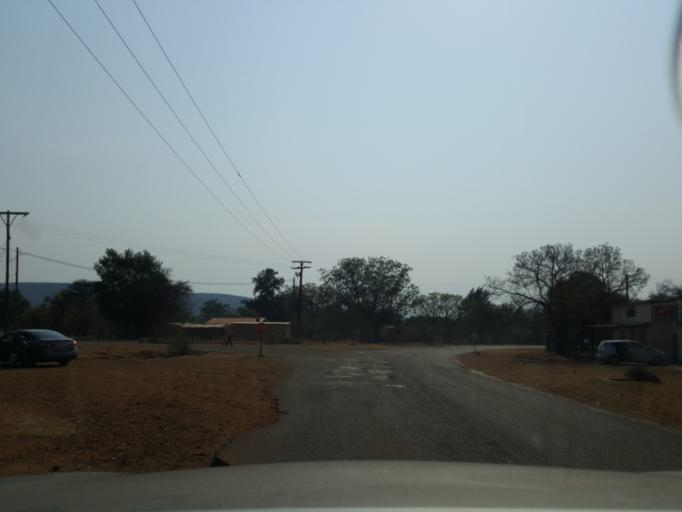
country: BW
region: South East
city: Lobatse
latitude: -25.3126
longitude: 25.8008
